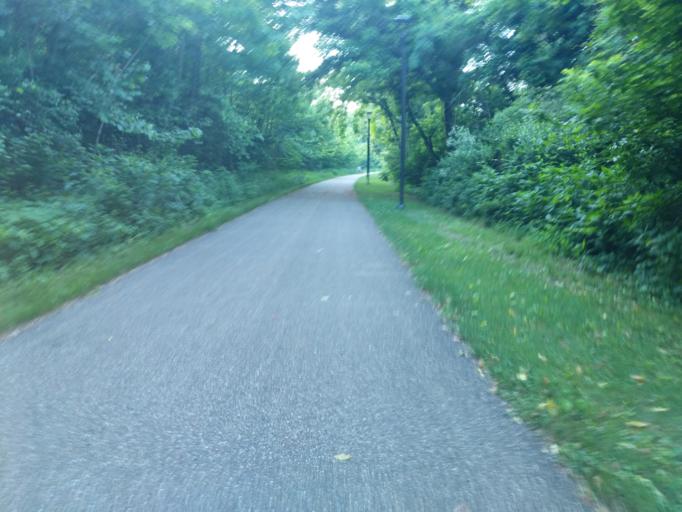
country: US
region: Ohio
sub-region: Athens County
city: Nelsonville
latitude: 39.4346
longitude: -82.2147
